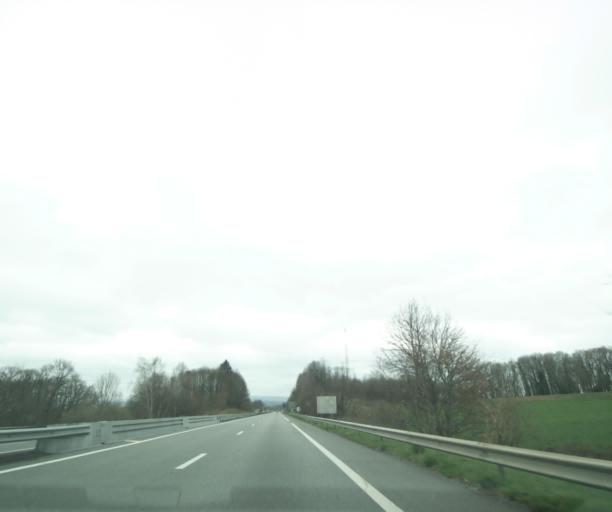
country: FR
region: Limousin
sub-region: Departement de la Creuse
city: Saint-Maurice-la-Souterraine
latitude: 46.2001
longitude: 1.3823
